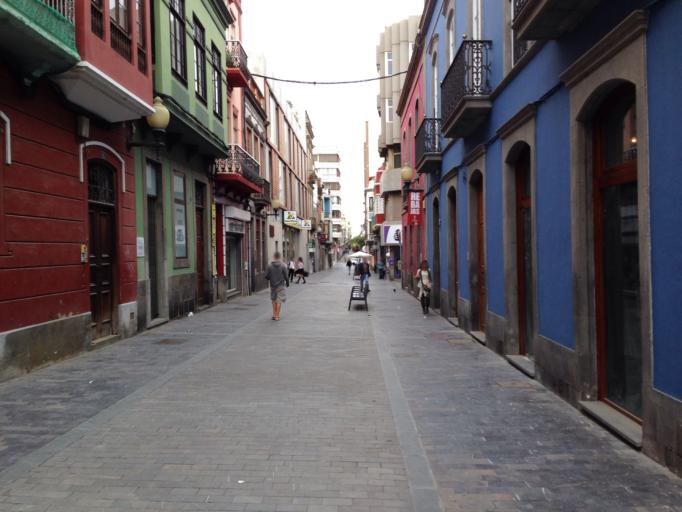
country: ES
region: Canary Islands
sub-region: Provincia de Las Palmas
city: Las Palmas de Gran Canaria
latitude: 28.1043
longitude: -15.4176
